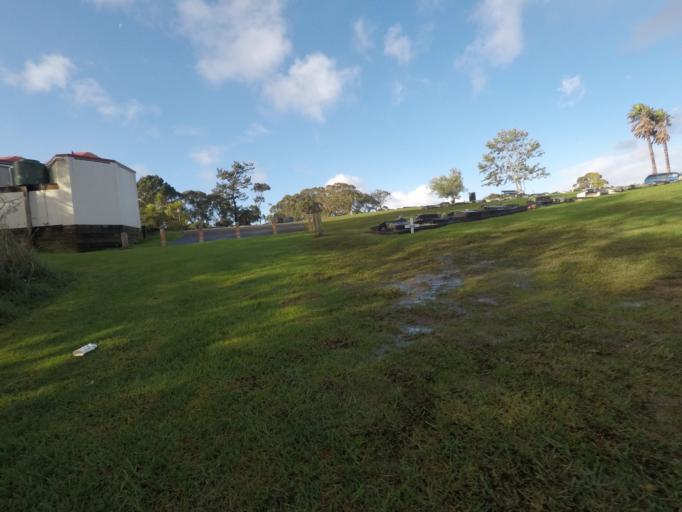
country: NZ
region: Auckland
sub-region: Auckland
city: Waitakere
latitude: -36.9039
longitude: 174.6415
